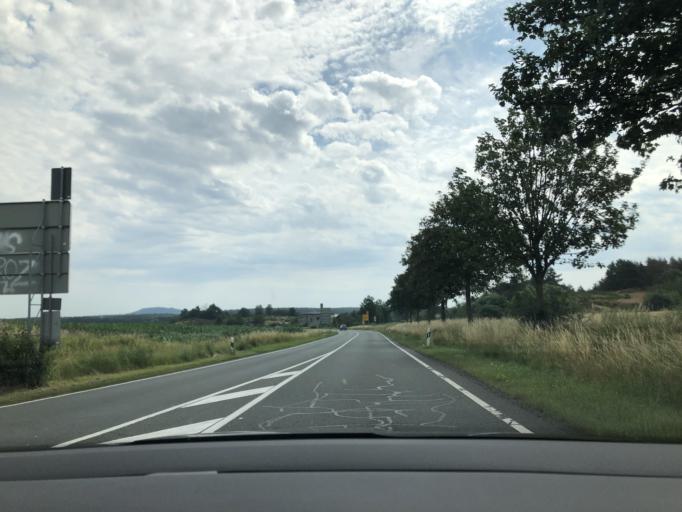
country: DE
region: Saxony-Anhalt
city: Blankenburg
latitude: 51.8240
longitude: 10.9269
